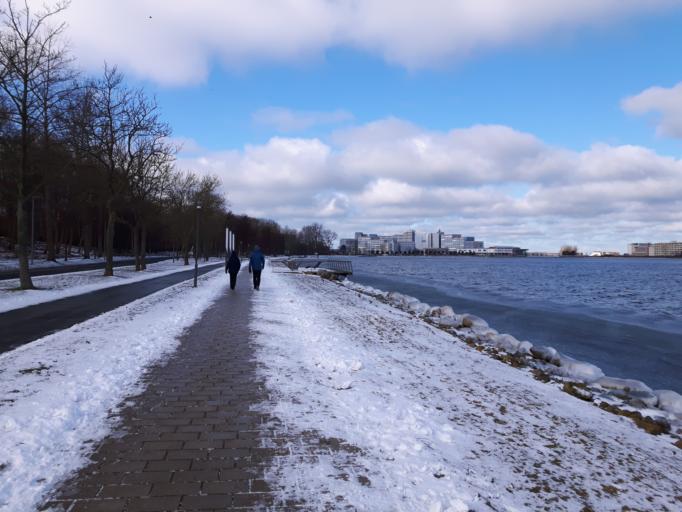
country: DE
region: Schleswig-Holstein
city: Heiligenhafen
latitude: 54.3749
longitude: 10.9645
